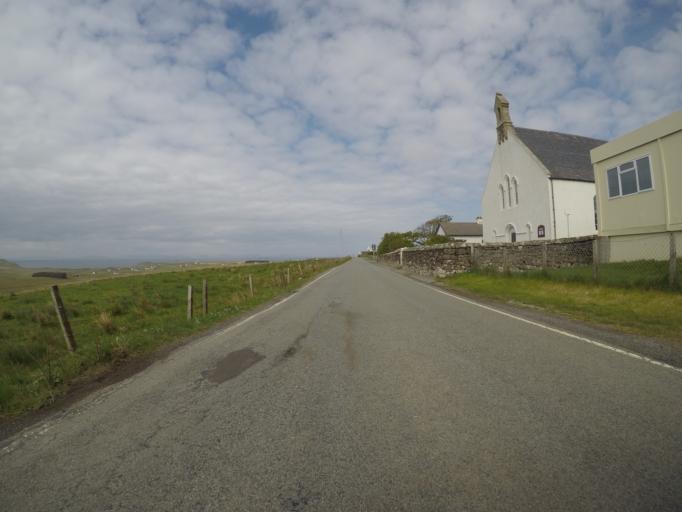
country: GB
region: Scotland
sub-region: Highland
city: Portree
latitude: 57.6360
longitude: -6.3764
